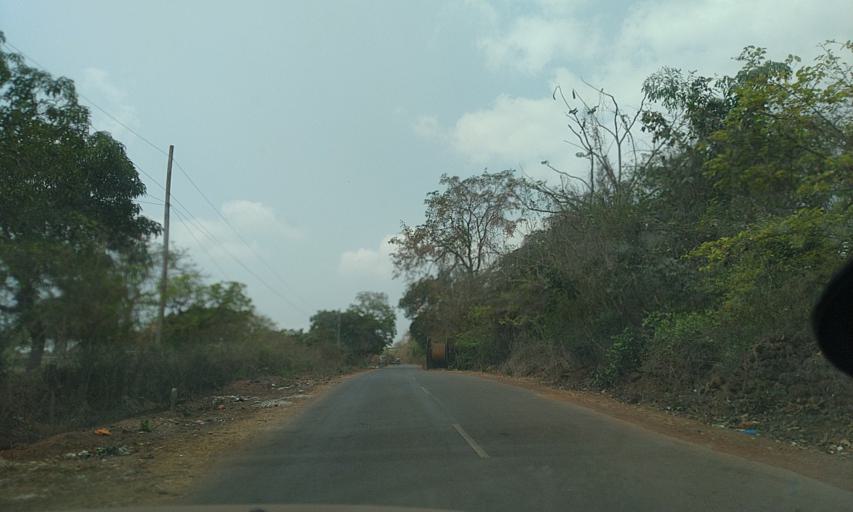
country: IN
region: Goa
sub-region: North Goa
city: Jua
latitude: 15.4934
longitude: 73.9101
